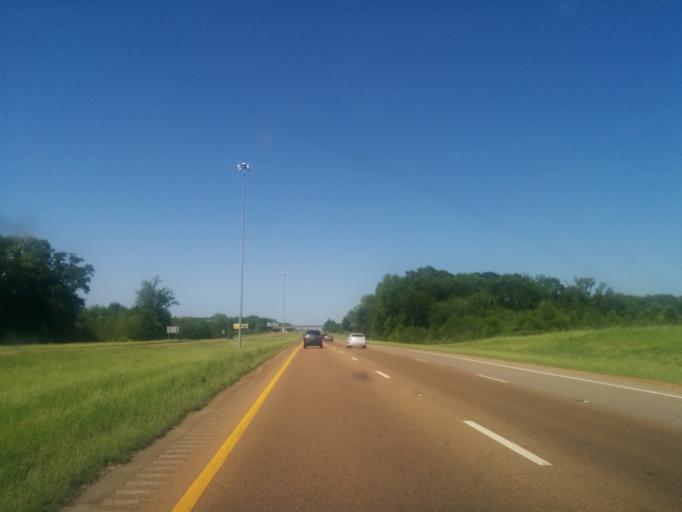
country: US
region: Mississippi
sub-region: Madison County
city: Madison
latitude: 32.5445
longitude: -90.0927
